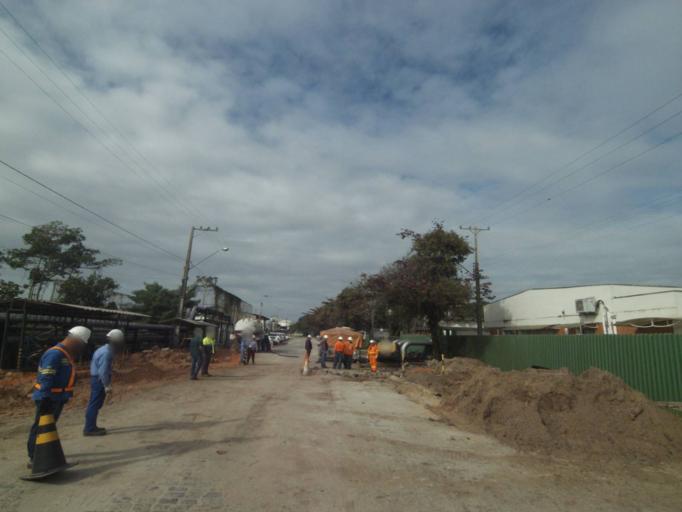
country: BR
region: Parana
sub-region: Paranagua
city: Paranagua
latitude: -25.5062
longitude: -48.5340
